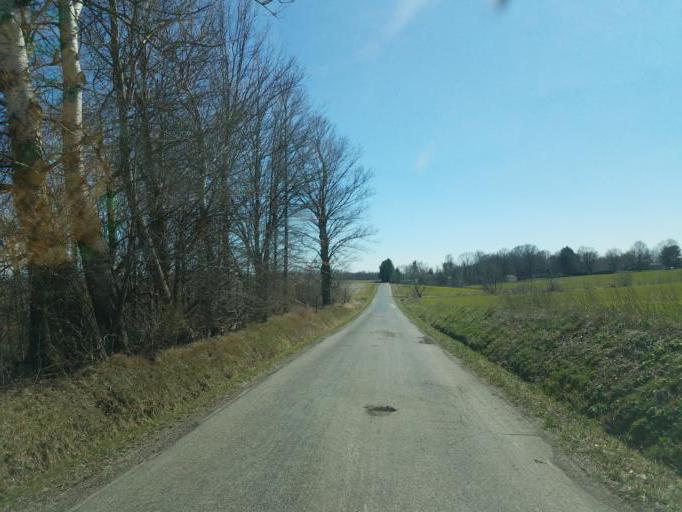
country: US
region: Ohio
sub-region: Ashland County
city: Ashland
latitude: 40.8739
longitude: -82.4067
